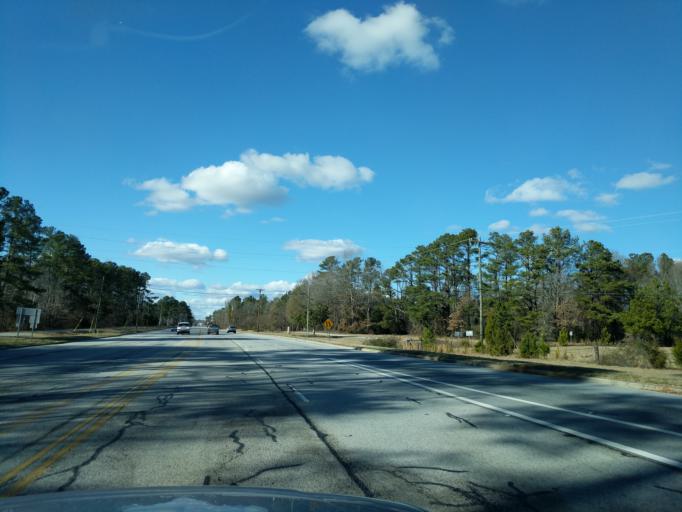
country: US
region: South Carolina
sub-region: Greenwood County
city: Greenwood
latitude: 34.1155
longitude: -82.1104
